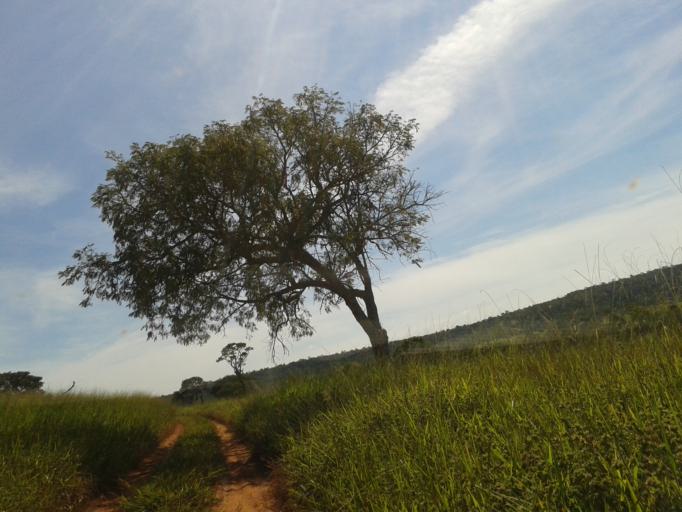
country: BR
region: Minas Gerais
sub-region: Campina Verde
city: Campina Verde
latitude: -19.4358
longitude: -49.6959
